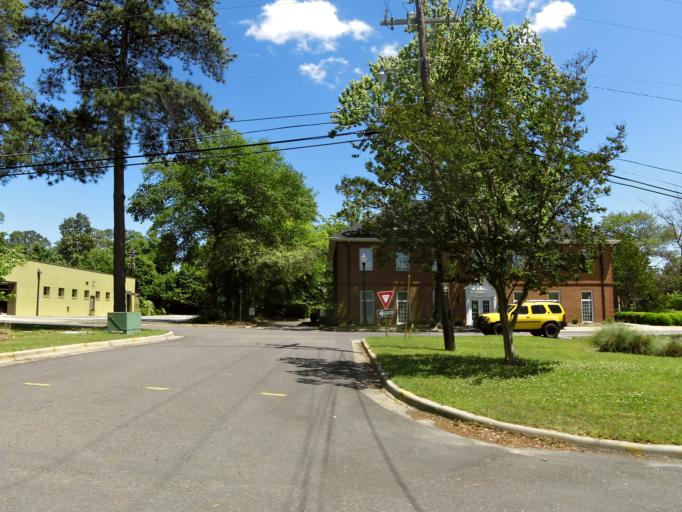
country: US
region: South Carolina
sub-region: Aiken County
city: Aiken
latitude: 33.5595
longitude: -81.7200
